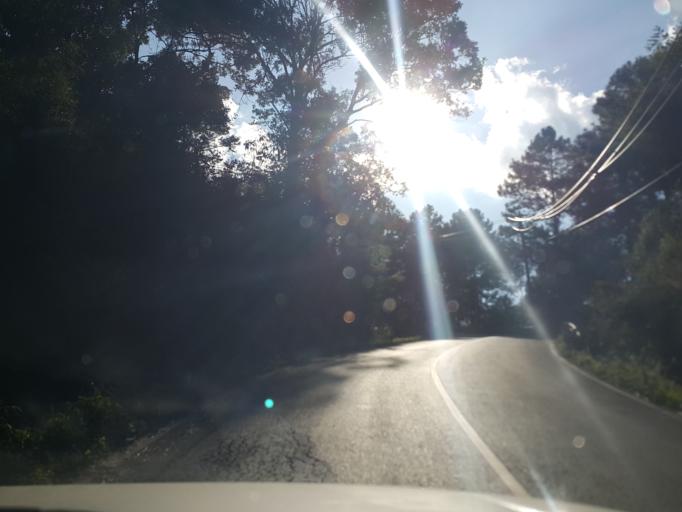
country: TH
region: Chiang Mai
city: Mae Chaem
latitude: 18.6383
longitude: 98.5183
